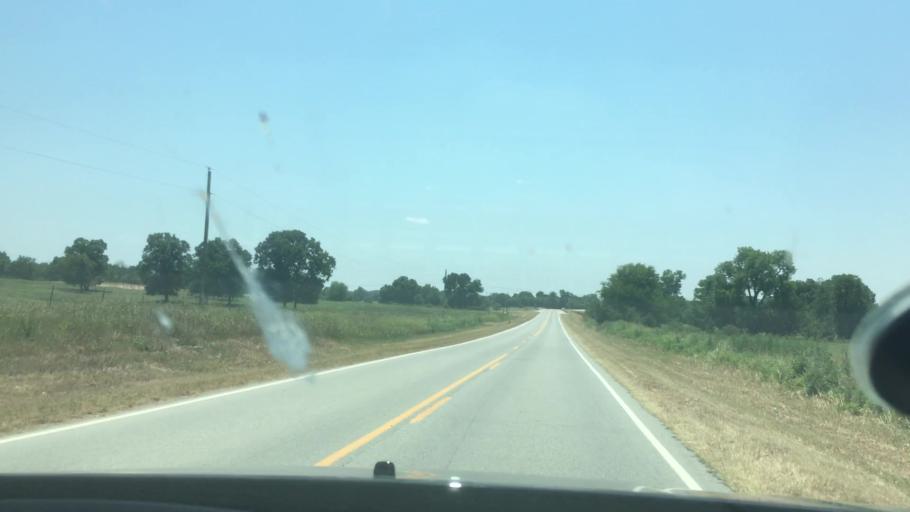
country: US
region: Oklahoma
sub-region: Coal County
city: Coalgate
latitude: 34.5530
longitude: -96.4070
